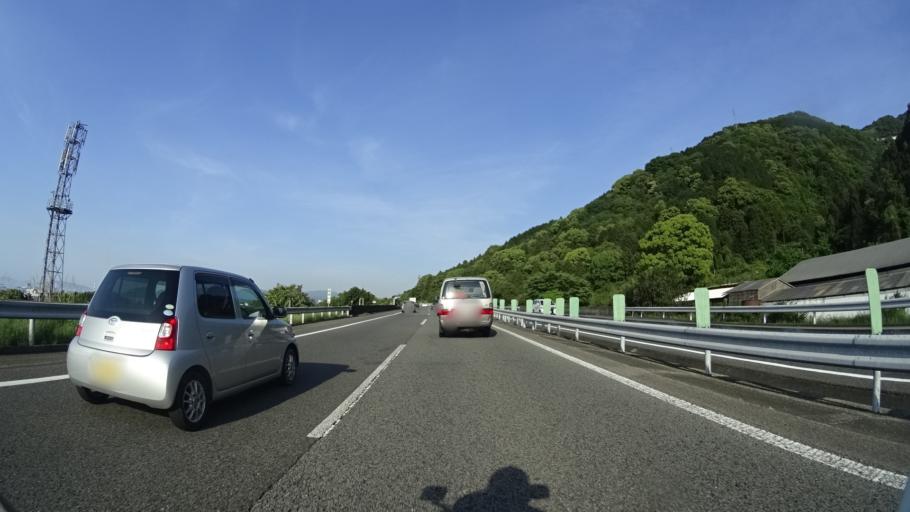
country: JP
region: Ehime
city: Kawanoecho
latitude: 33.9622
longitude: 133.5198
